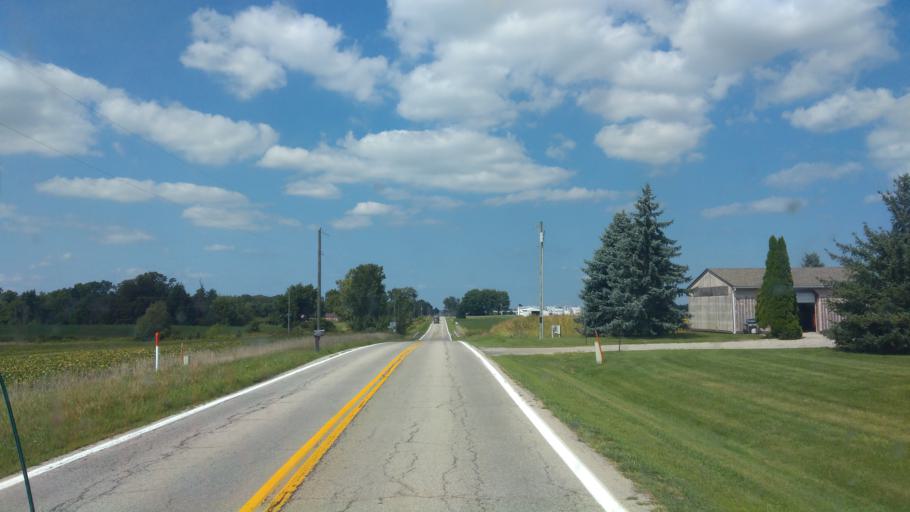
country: US
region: Ohio
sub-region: Union County
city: Marysville
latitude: 40.3630
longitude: -83.4546
